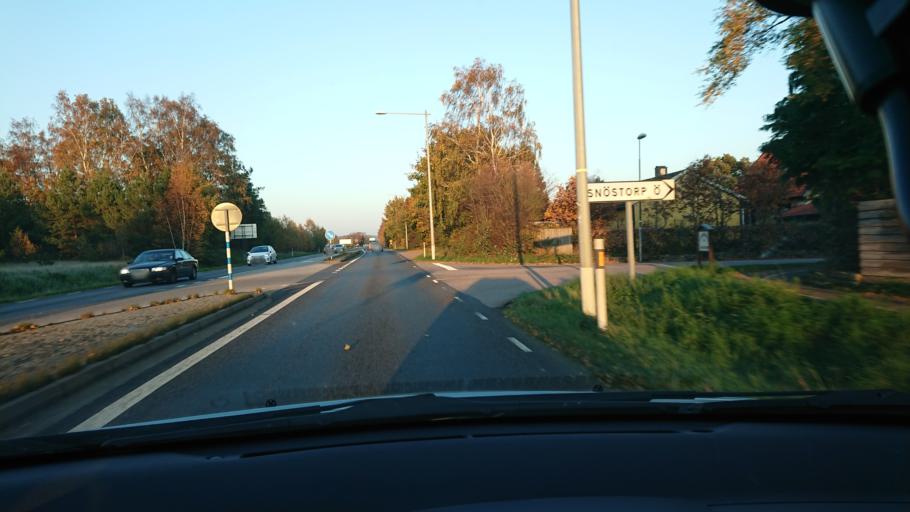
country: SE
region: Halland
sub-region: Halmstads Kommun
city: Fyllinge
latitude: 56.6794
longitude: 12.9295
